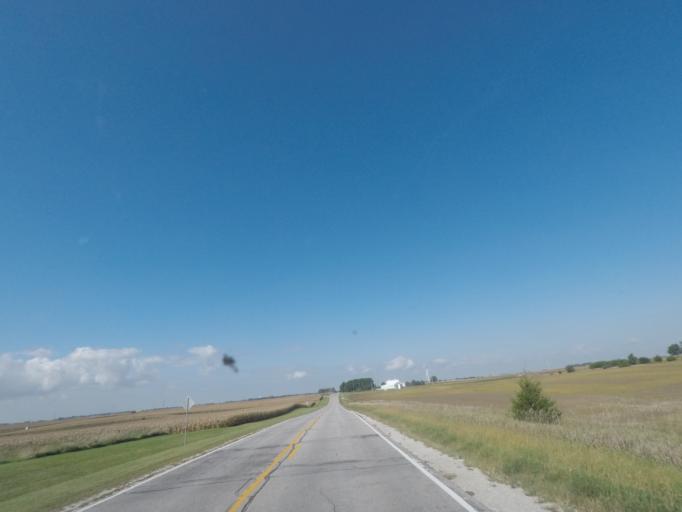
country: US
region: Iowa
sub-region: Story County
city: Nevada
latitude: 42.0226
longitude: -93.4008
